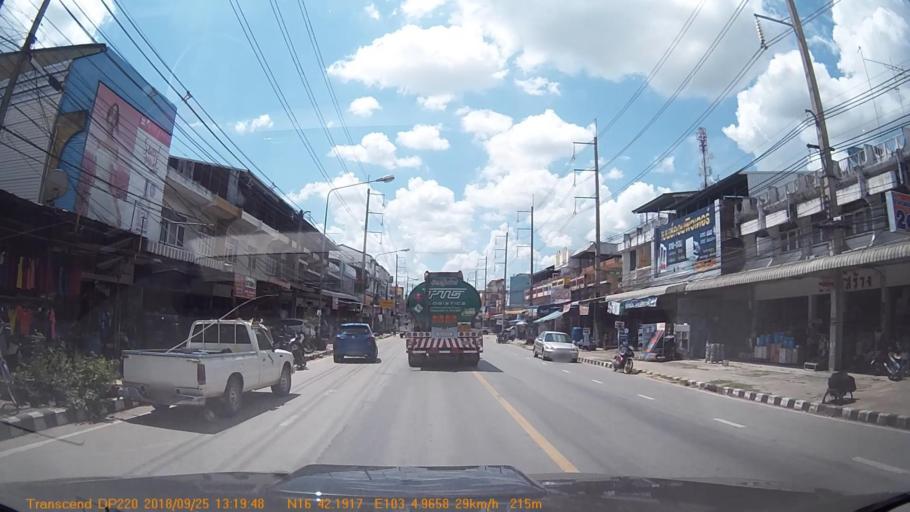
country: TH
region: Khon Kaen
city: Kranuan
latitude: 16.7032
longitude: 103.0827
